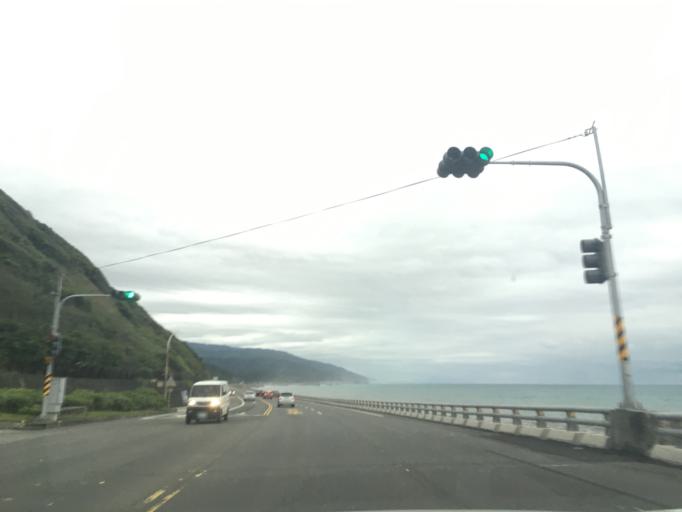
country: TW
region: Taiwan
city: Hengchun
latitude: 22.3103
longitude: 120.8908
